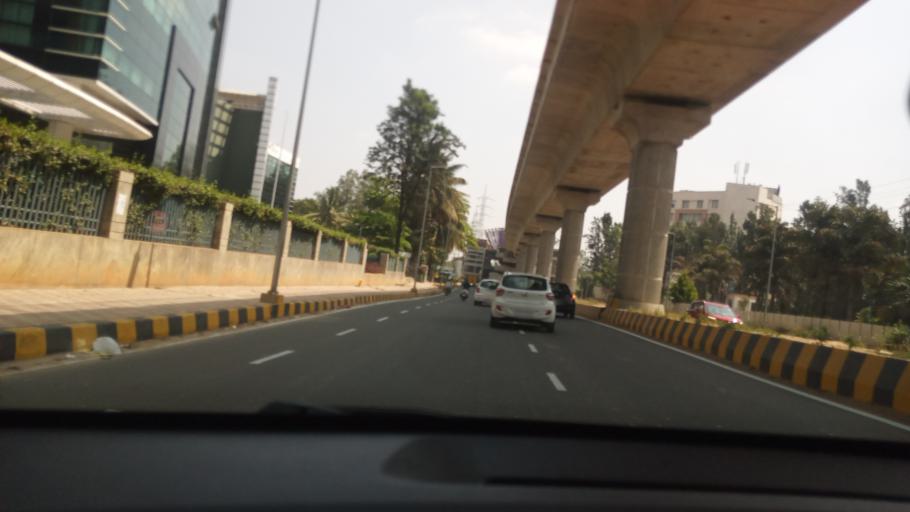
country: IN
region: Karnataka
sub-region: Bangalore Urban
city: Bangalore
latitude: 12.9780
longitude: 77.7128
